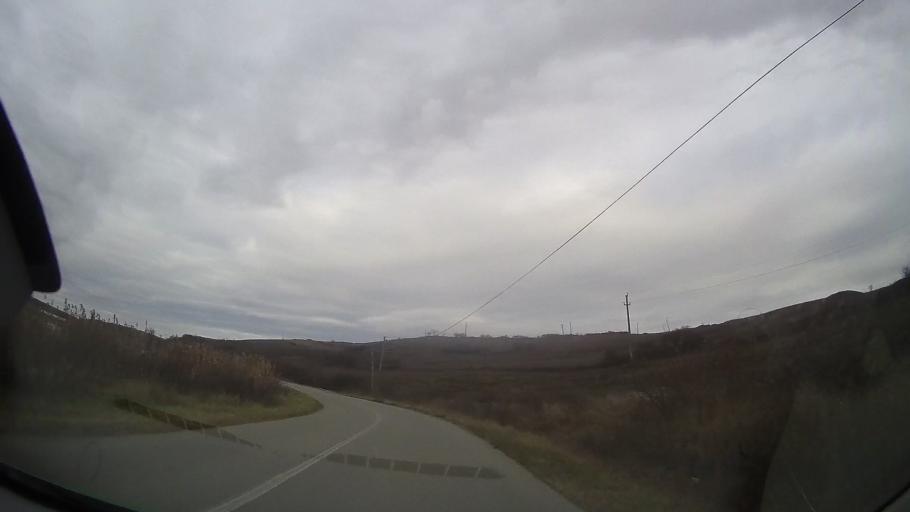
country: RO
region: Mures
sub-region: Comuna Faragau
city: Faragau
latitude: 46.7484
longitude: 24.5288
